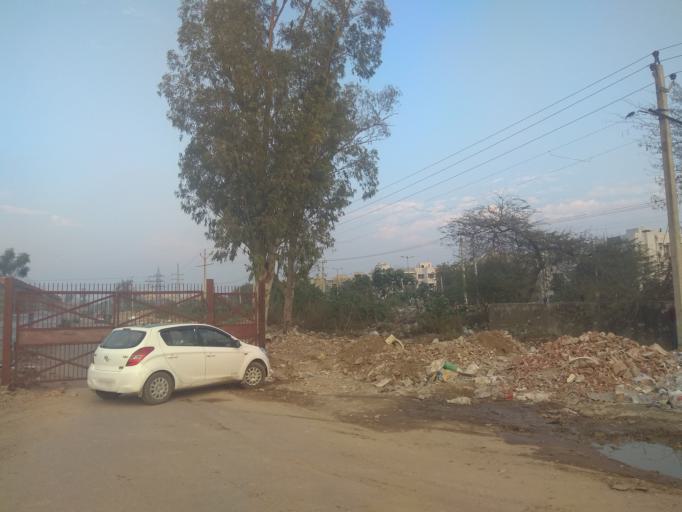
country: IN
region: NCT
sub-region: West Delhi
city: Nangloi Jat
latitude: 28.6396
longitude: 77.0612
